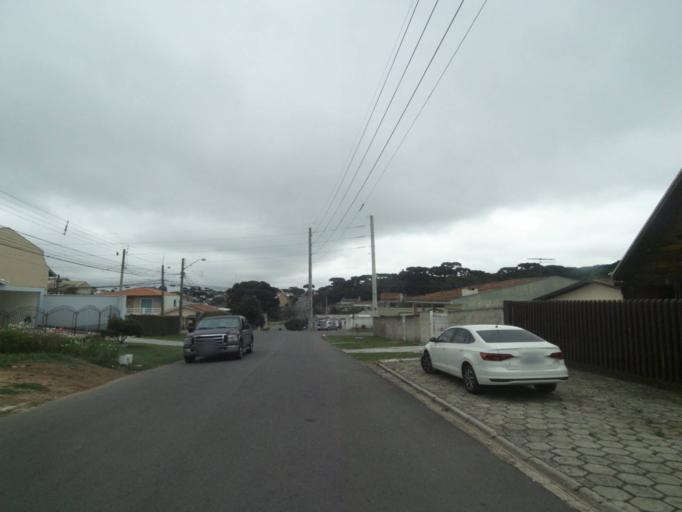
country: BR
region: Parana
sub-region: Sao Jose Dos Pinhais
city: Sao Jose dos Pinhais
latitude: -25.5380
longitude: -49.2845
